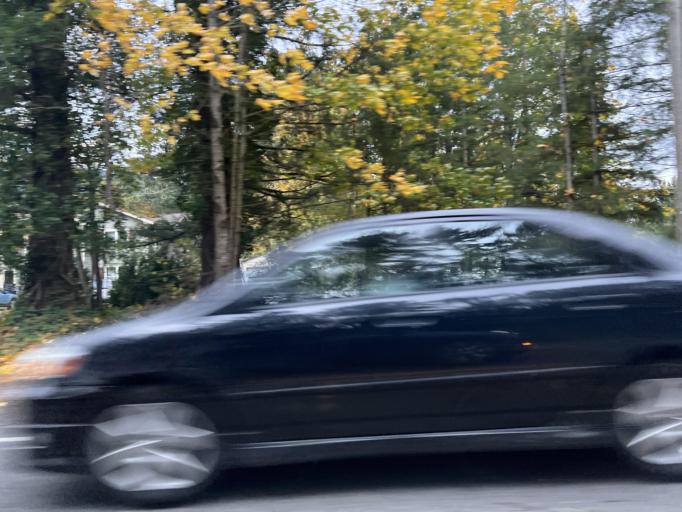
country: US
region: Washington
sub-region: King County
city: Tanner
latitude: 47.4773
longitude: -121.7583
